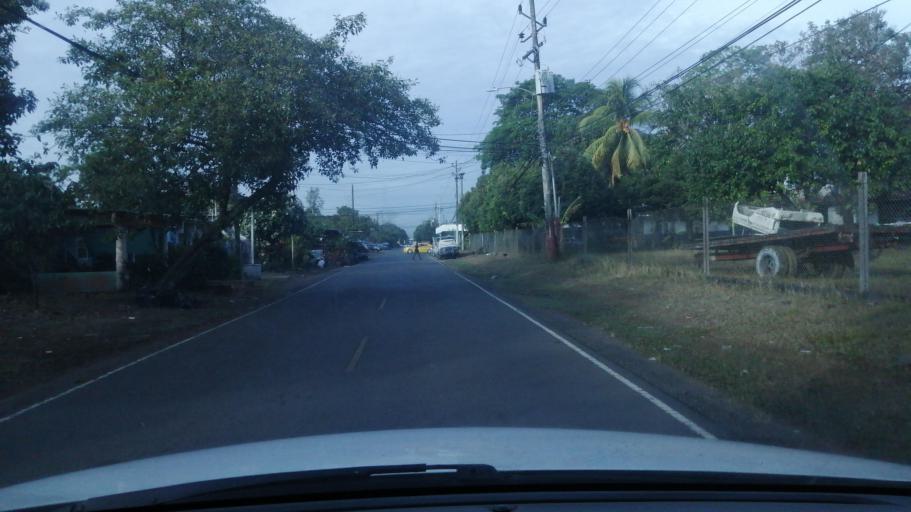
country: PA
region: Chiriqui
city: David
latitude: 8.4386
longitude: -82.4354
